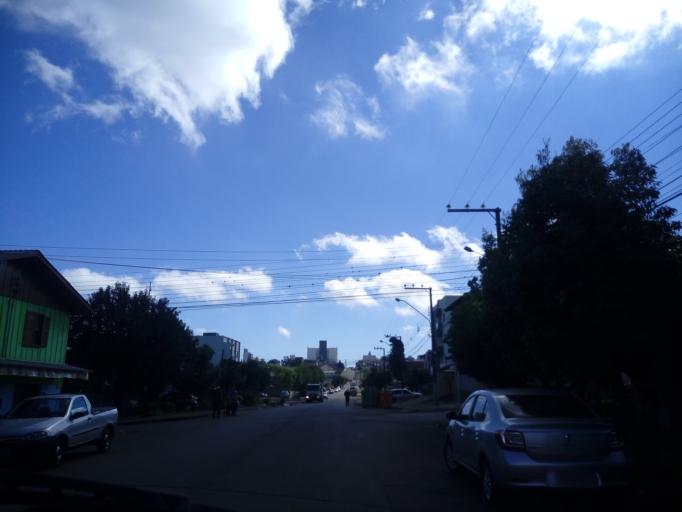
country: BR
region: Santa Catarina
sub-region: Chapeco
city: Chapeco
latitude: -27.1107
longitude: -52.6030
